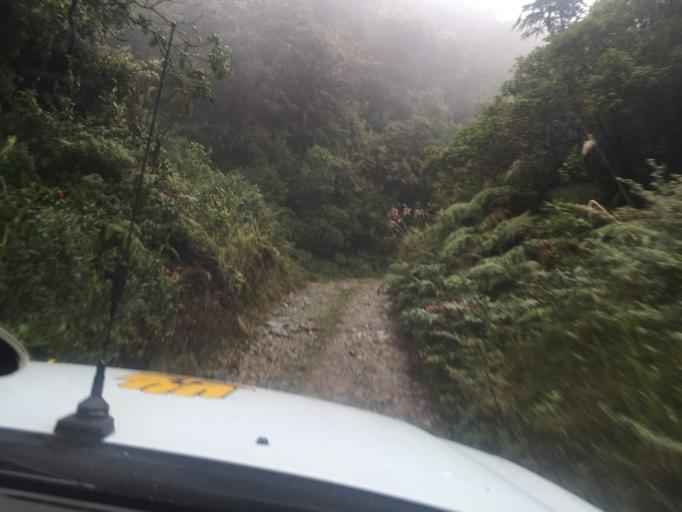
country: CO
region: Quindio
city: Calarca
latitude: 4.4740
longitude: -75.5627
